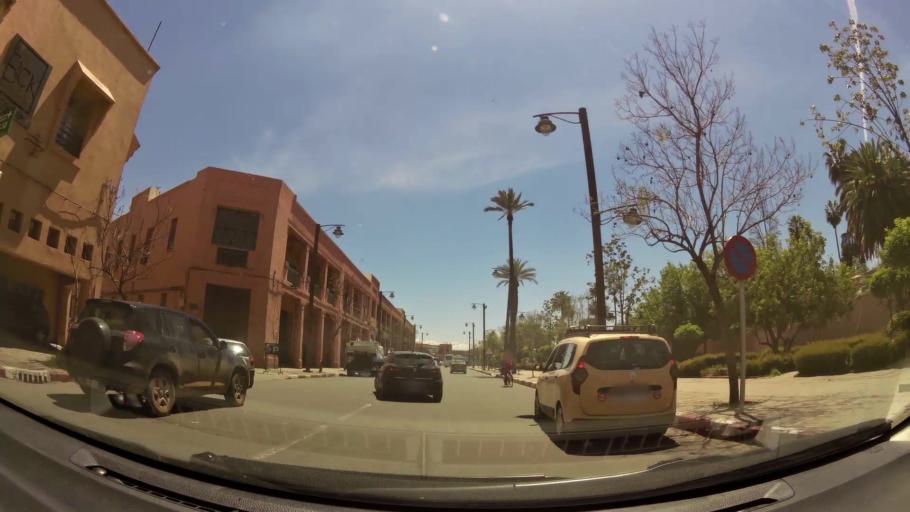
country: MA
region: Marrakech-Tensift-Al Haouz
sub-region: Marrakech
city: Marrakesh
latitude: 31.6237
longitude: -7.9919
